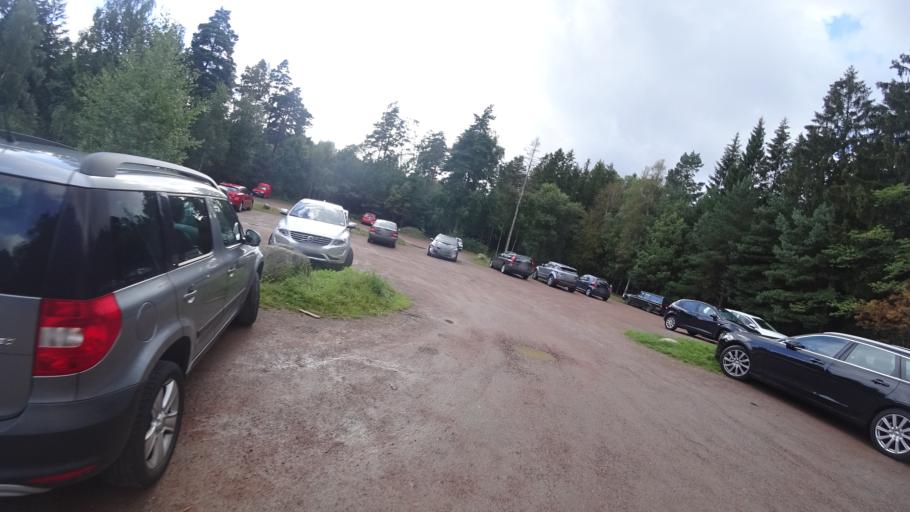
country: SE
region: Vaestra Goetaland
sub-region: Partille Kommun
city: Ojersjo
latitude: 57.6807
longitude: 12.0878
